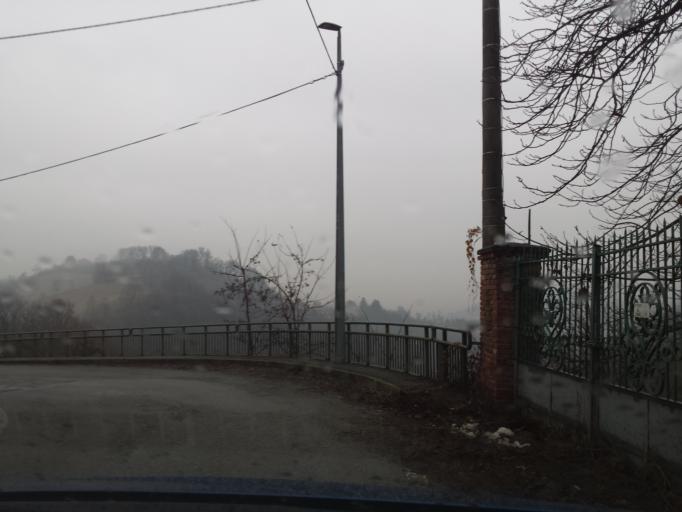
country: IT
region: Piedmont
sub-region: Provincia di Torino
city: Revigliasco
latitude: 45.0533
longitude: 7.7331
